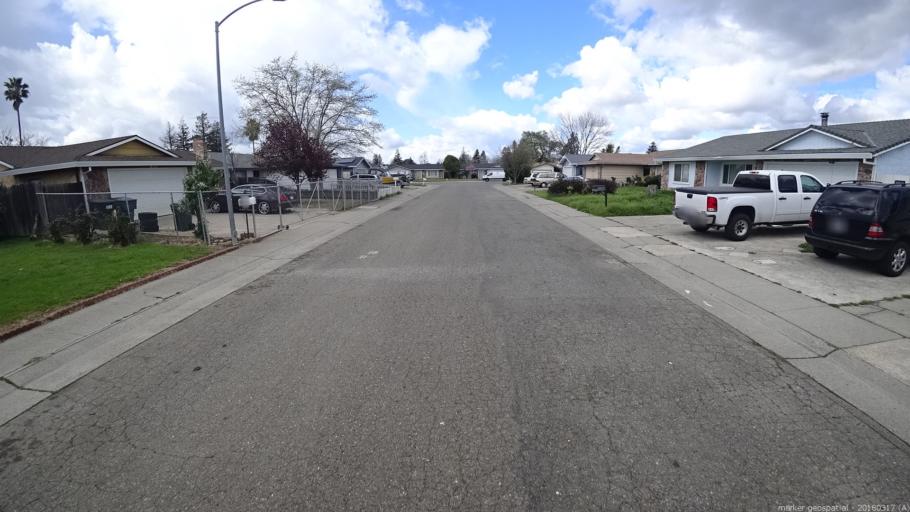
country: US
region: California
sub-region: Sacramento County
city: Florin
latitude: 38.4798
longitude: -121.4011
